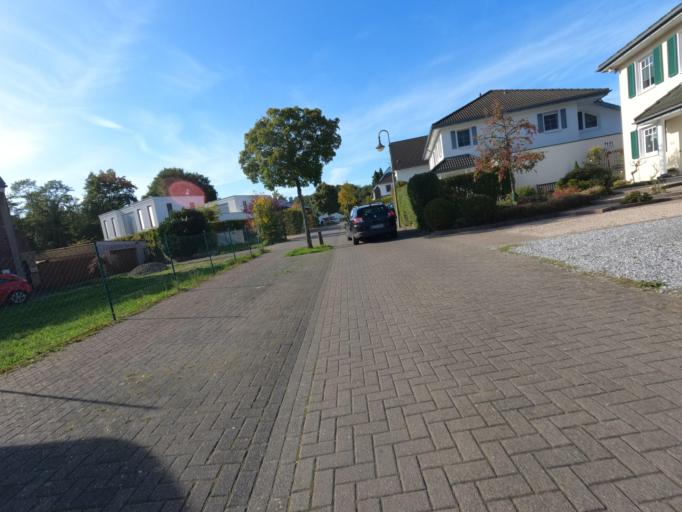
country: DE
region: North Rhine-Westphalia
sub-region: Regierungsbezirk Dusseldorf
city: Niederkruchten
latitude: 51.1512
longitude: 6.2022
